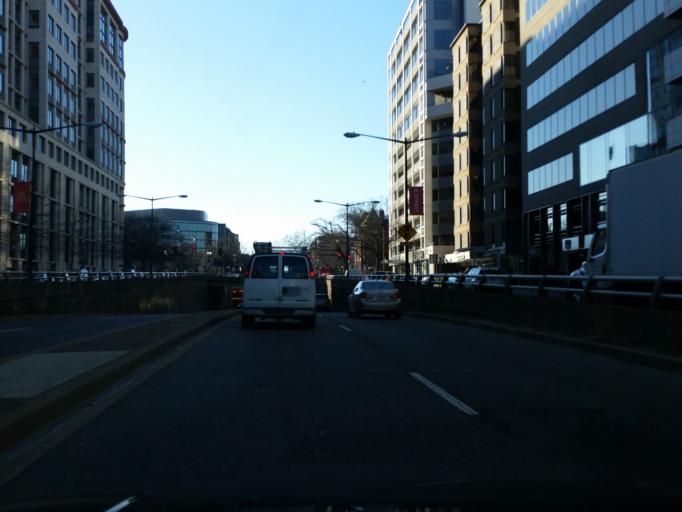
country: US
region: Washington, D.C.
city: Washington, D.C.
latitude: 38.9026
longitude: -77.0471
